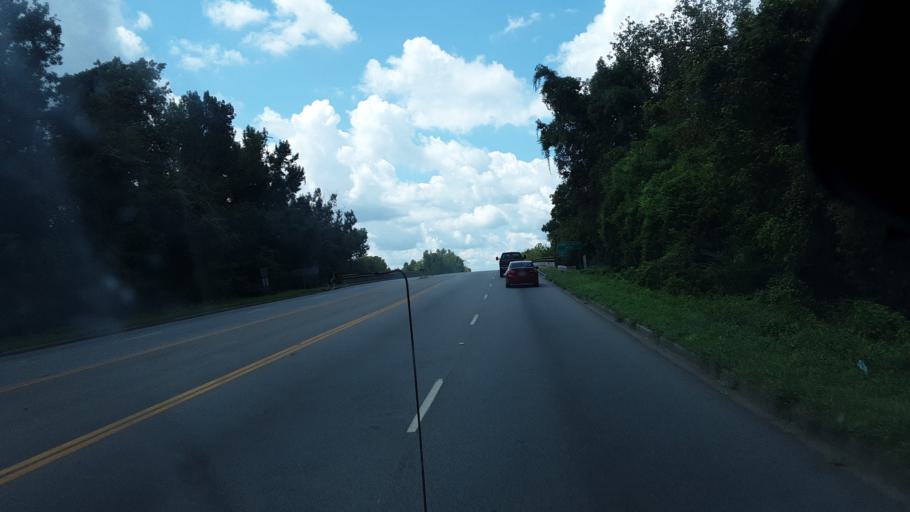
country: US
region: South Carolina
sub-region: Berkeley County
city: Moncks Corner
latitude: 33.2160
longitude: -79.9733
